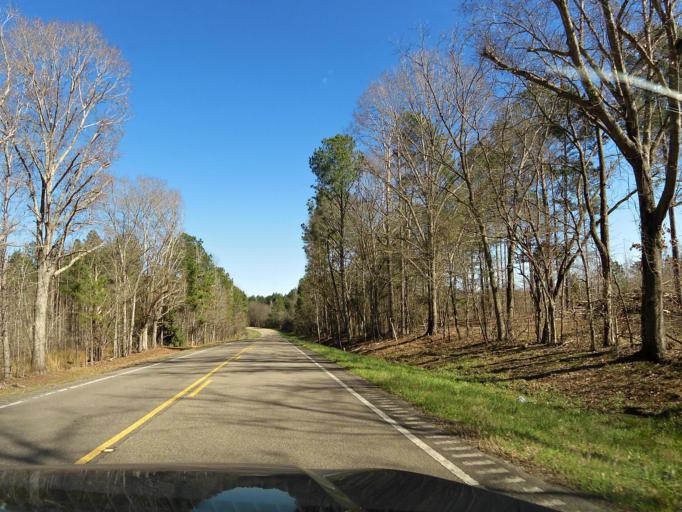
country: US
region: Alabama
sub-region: Bullock County
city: Union Springs
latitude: 32.1109
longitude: -85.7910
